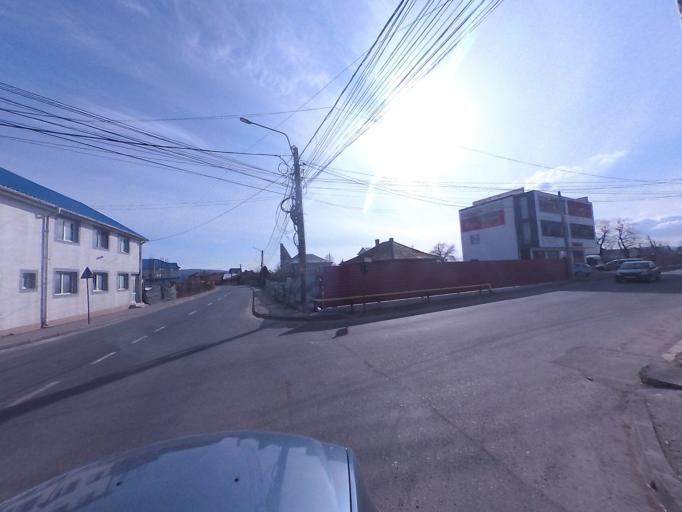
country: RO
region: Neamt
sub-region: Oras Targu Neamt
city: Targu Neamt
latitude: 47.2037
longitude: 26.3628
